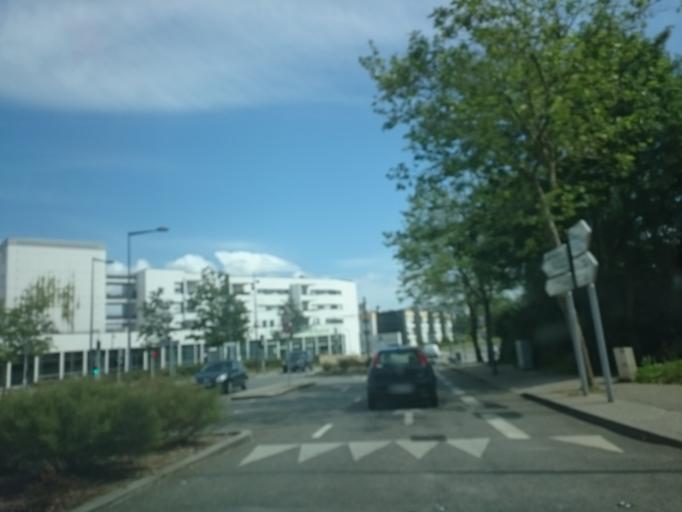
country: FR
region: Brittany
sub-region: Departement du Finistere
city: Brest
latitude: 48.4108
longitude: -4.4716
